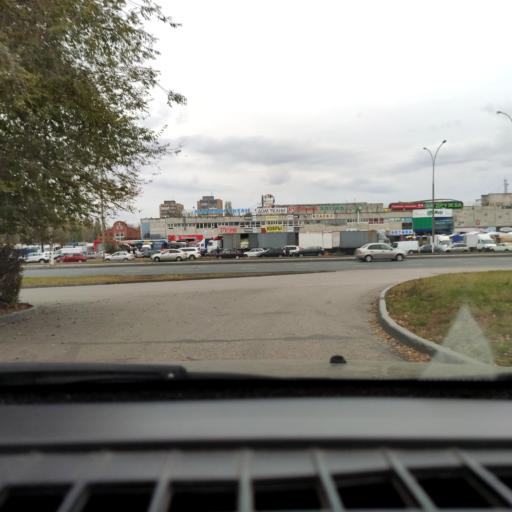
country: RU
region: Samara
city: Tol'yatti
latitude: 53.5308
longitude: 49.2653
